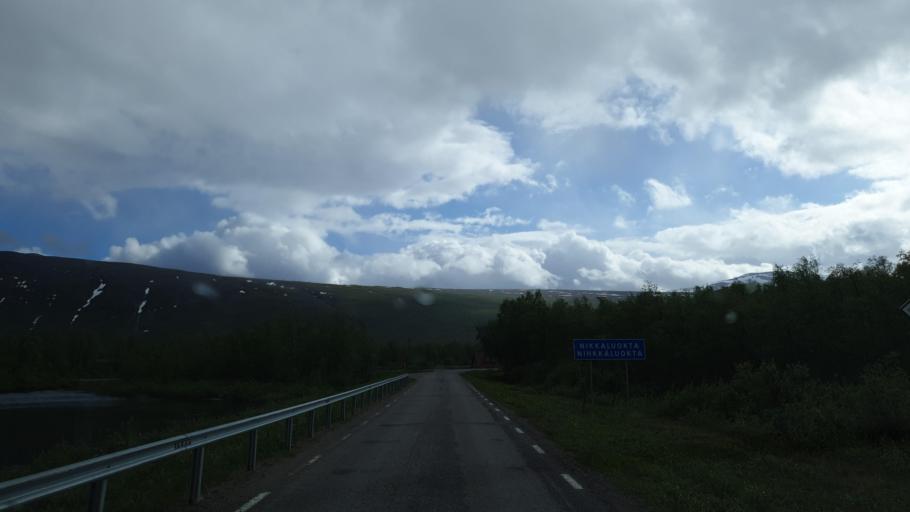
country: SE
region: Norrbotten
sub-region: Kiruna Kommun
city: Kiruna
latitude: 67.8525
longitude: 19.0181
